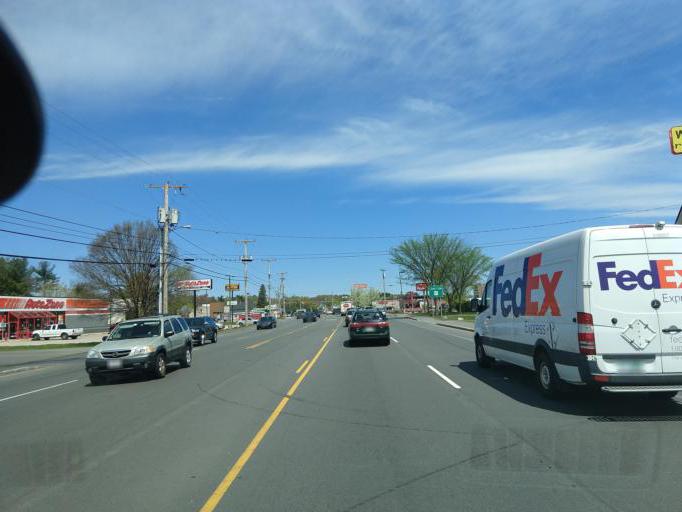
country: US
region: New Hampshire
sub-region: Rockingham County
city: Seabrook
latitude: 42.8895
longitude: -70.8716
